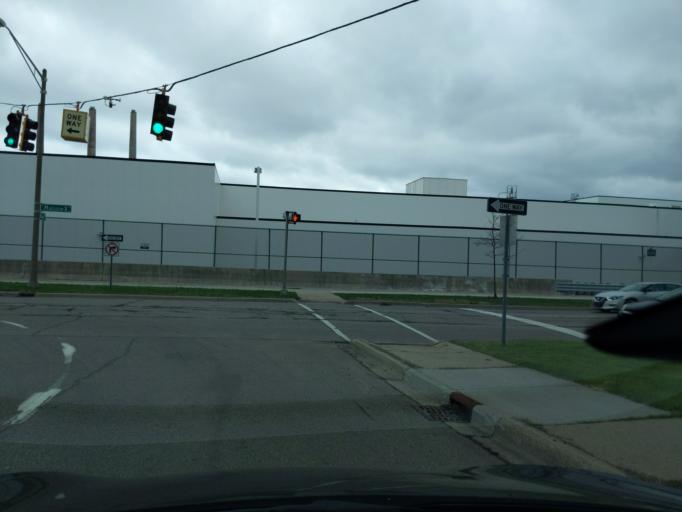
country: US
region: Michigan
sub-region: Ingham County
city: Lansing
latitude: 42.7257
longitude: -84.5602
